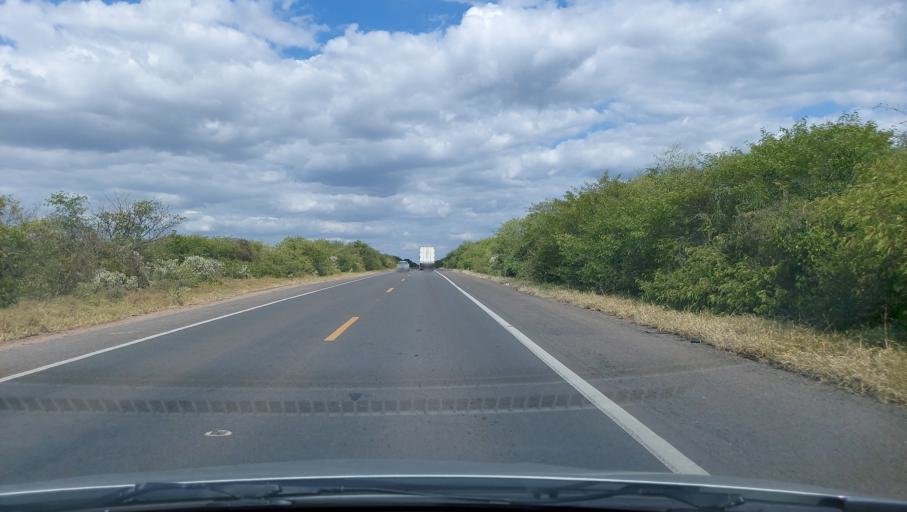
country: BR
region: Bahia
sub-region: Ipira
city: Ipira
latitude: -12.4885
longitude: -39.7923
